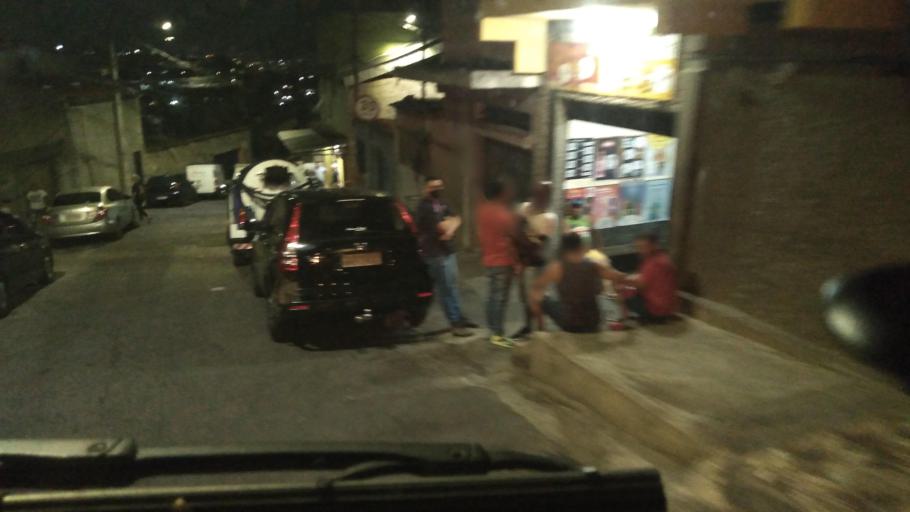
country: BR
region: Minas Gerais
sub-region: Belo Horizonte
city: Belo Horizonte
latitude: -19.8829
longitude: -43.9527
